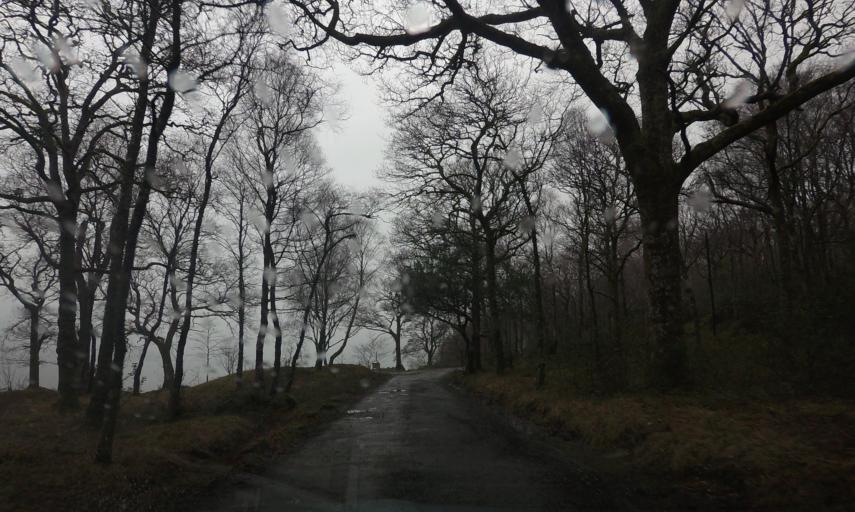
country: GB
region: Scotland
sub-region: West Dunbartonshire
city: Balloch
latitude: 56.1533
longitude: -4.6421
